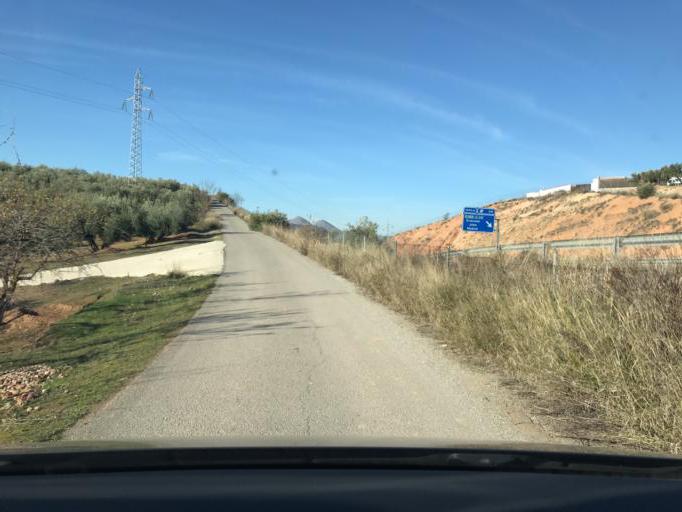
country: ES
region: Andalusia
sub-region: Provincia de Granada
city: Peligros
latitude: 37.2449
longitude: -3.6362
